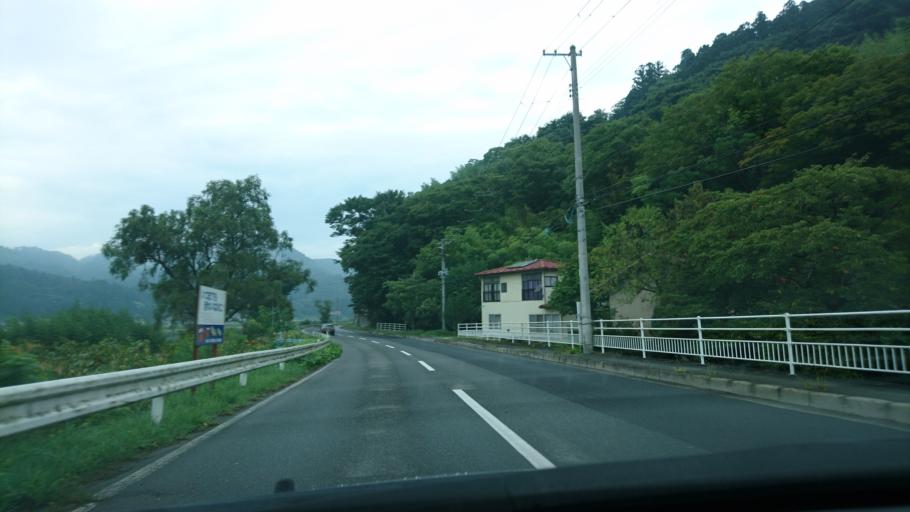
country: JP
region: Iwate
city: Ichinoseki
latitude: 38.9622
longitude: 141.2470
